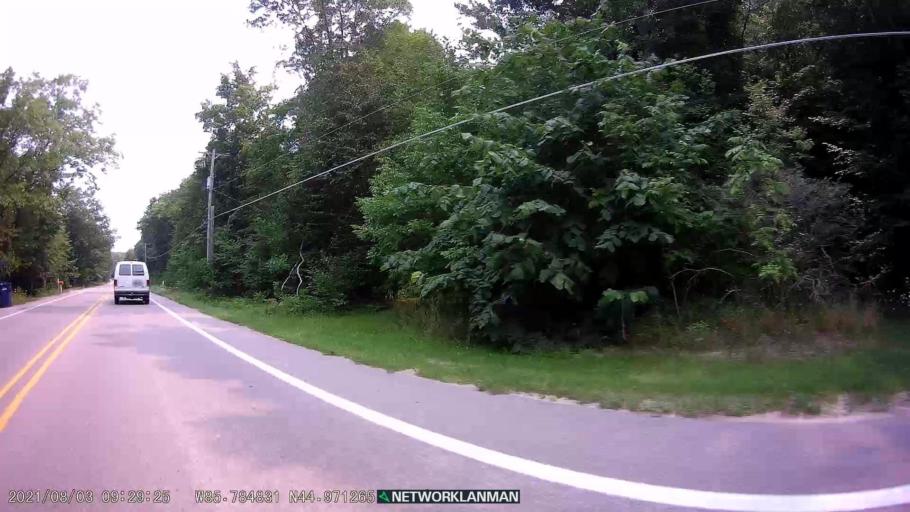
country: US
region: Michigan
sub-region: Leelanau County
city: Leland
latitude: 44.9714
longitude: -85.7847
